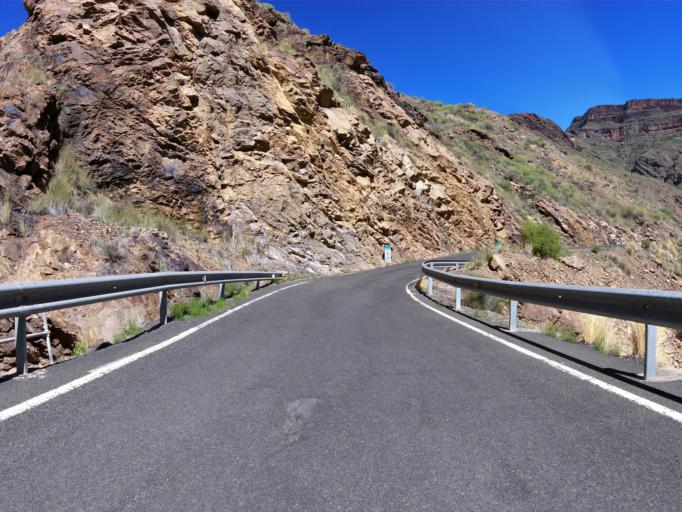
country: ES
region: Canary Islands
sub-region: Provincia de Las Palmas
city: Artenara
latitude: 27.9881
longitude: -15.6914
